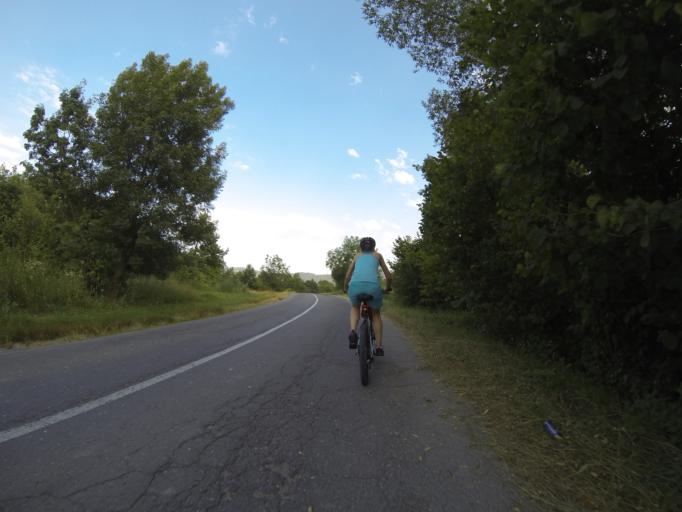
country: RO
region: Brasov
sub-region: Comuna Sinca Noua
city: Sinca Noua
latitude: 45.7254
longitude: 25.2364
